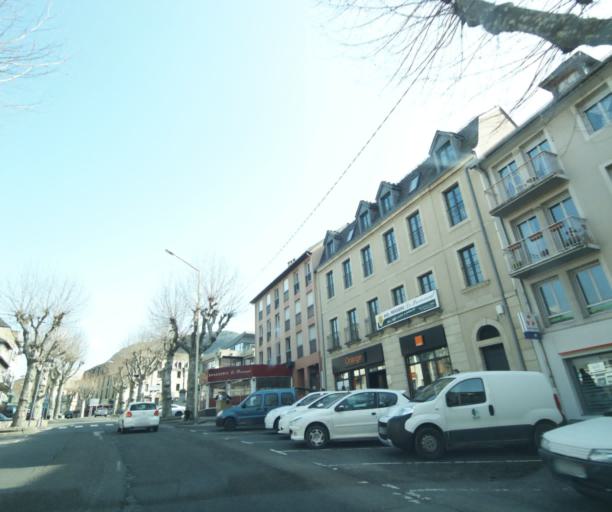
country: FR
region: Languedoc-Roussillon
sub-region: Departement de la Lozere
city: Mende
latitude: 44.5162
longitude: 3.4981
